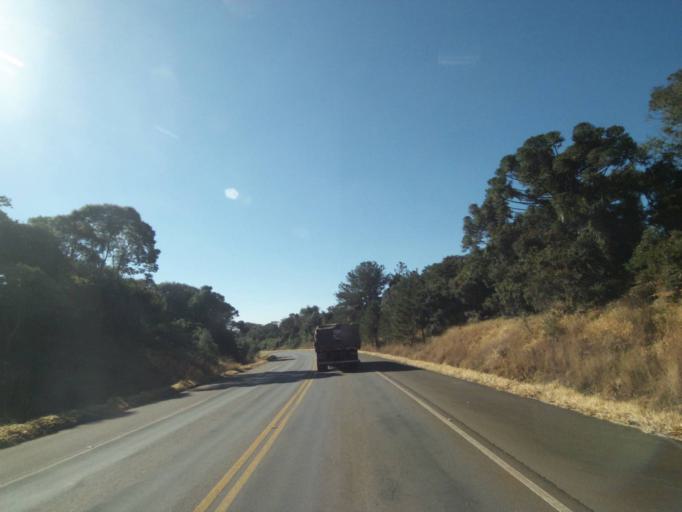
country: BR
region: Parana
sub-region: Tibagi
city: Tibagi
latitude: -24.6653
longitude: -50.4519
